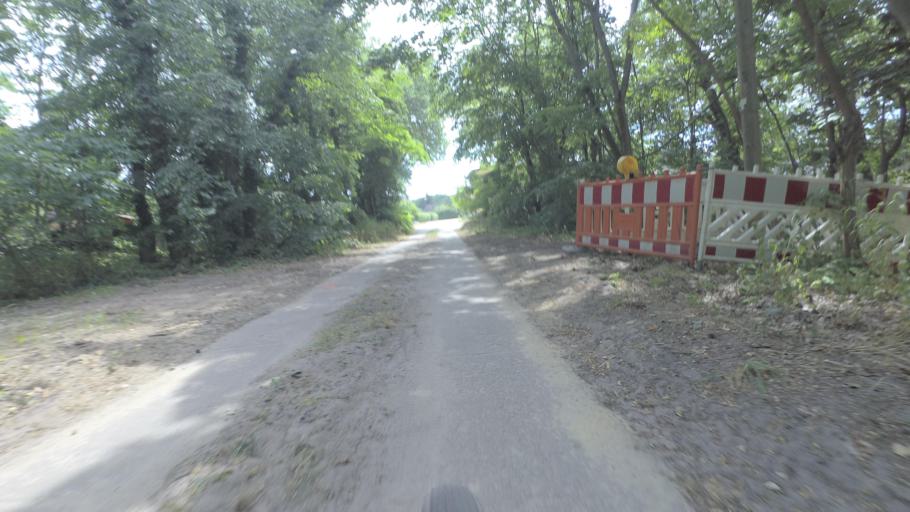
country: DE
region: Brandenburg
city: Stahnsdorf
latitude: 52.3401
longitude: 13.2258
